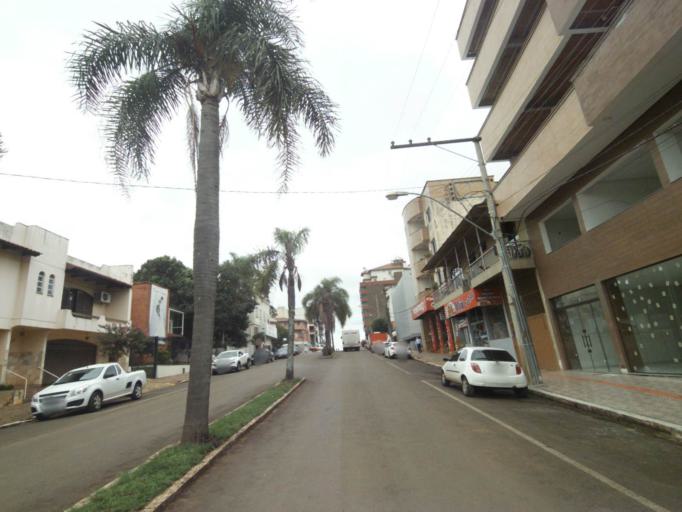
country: BR
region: Rio Grande do Sul
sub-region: Lagoa Vermelha
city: Lagoa Vermelha
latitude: -28.2095
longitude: -51.5228
